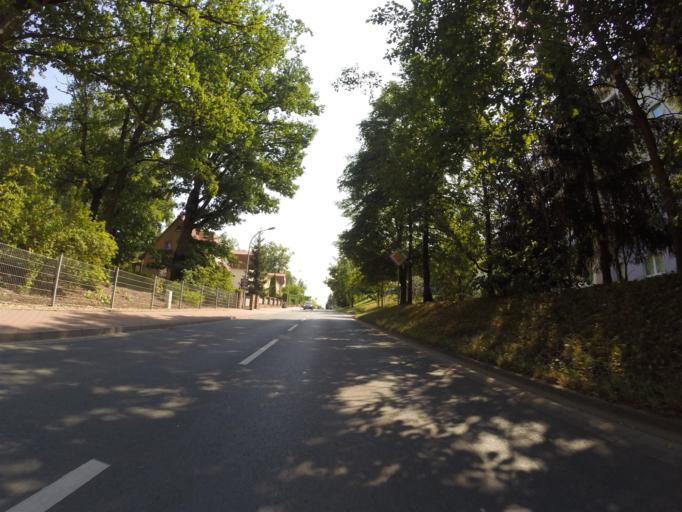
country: DE
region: Thuringia
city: Stadtroda
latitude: 50.8618
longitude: 11.7363
